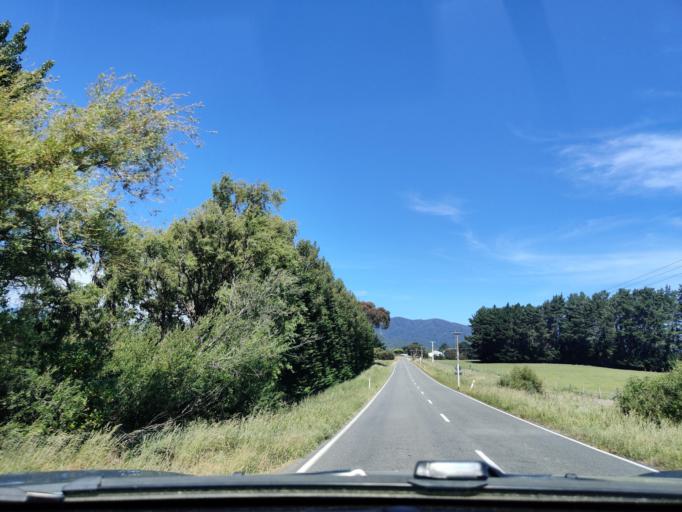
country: NZ
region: Wellington
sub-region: Upper Hutt City
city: Upper Hutt
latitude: -41.3273
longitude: 175.2291
